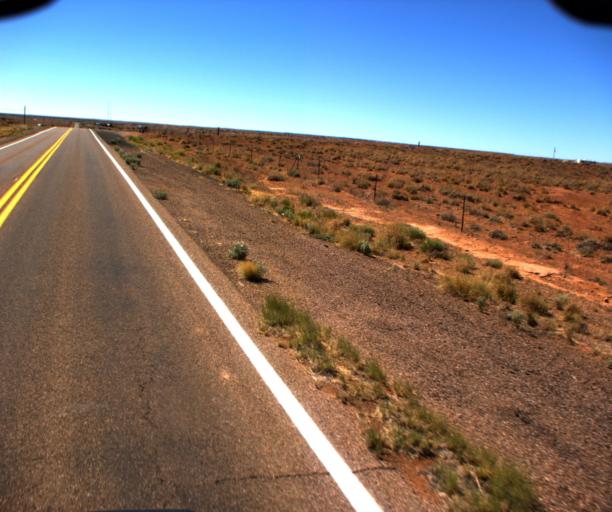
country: US
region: Arizona
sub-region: Navajo County
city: Winslow
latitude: 34.9925
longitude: -110.6689
